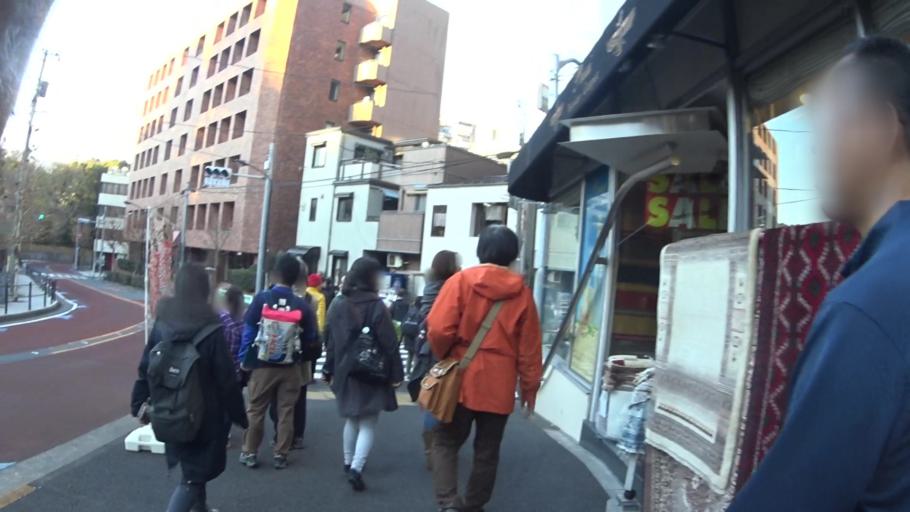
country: JP
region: Tokyo
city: Tokyo
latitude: 35.6768
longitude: 139.7333
